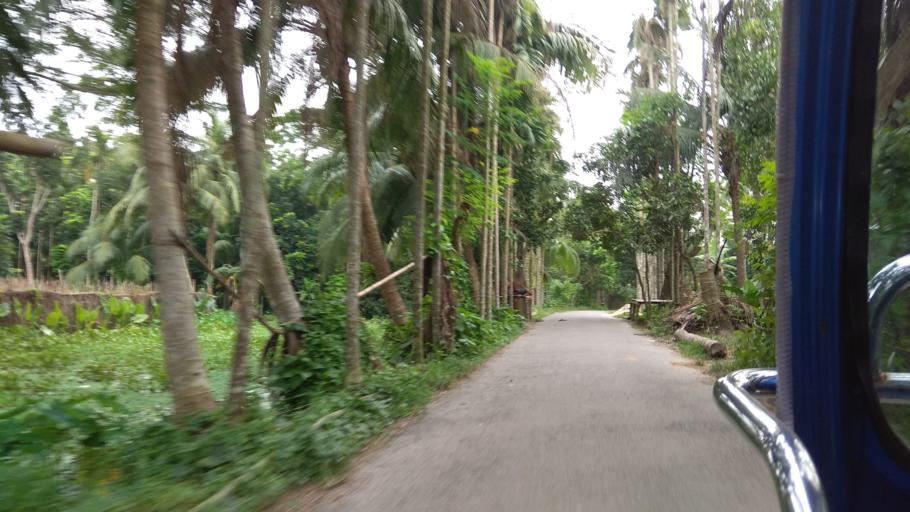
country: BD
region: Khulna
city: Kalia
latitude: 23.0352
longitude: 89.6565
